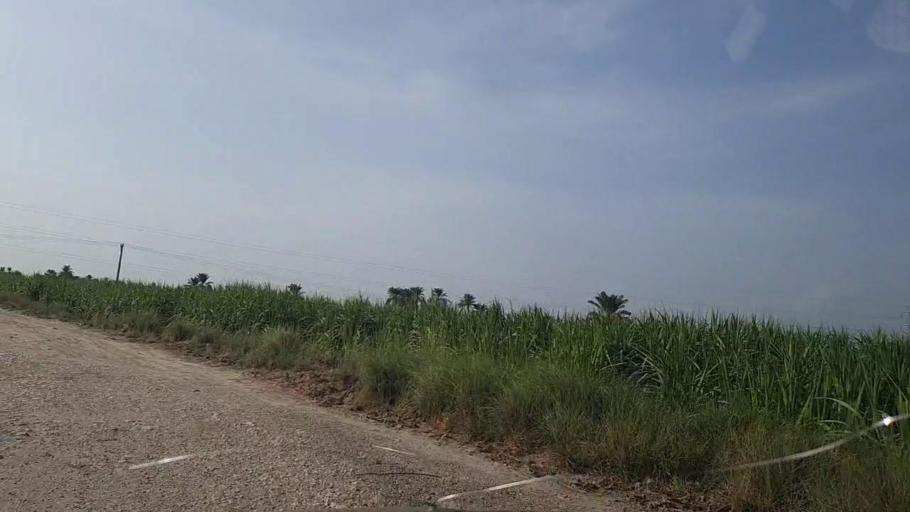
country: PK
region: Sindh
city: Ghotki
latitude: 28.0066
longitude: 69.2970
